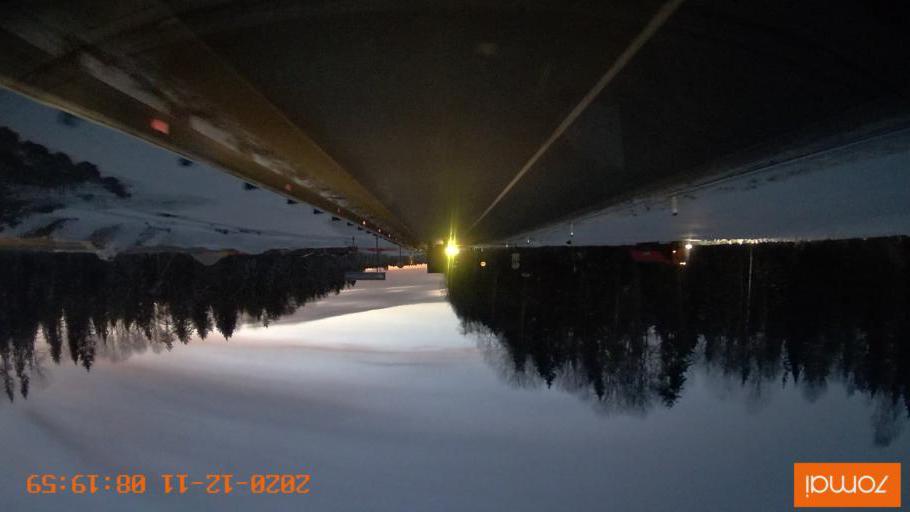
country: RU
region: Vologda
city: Molochnoye
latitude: 59.1465
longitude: 39.3506
